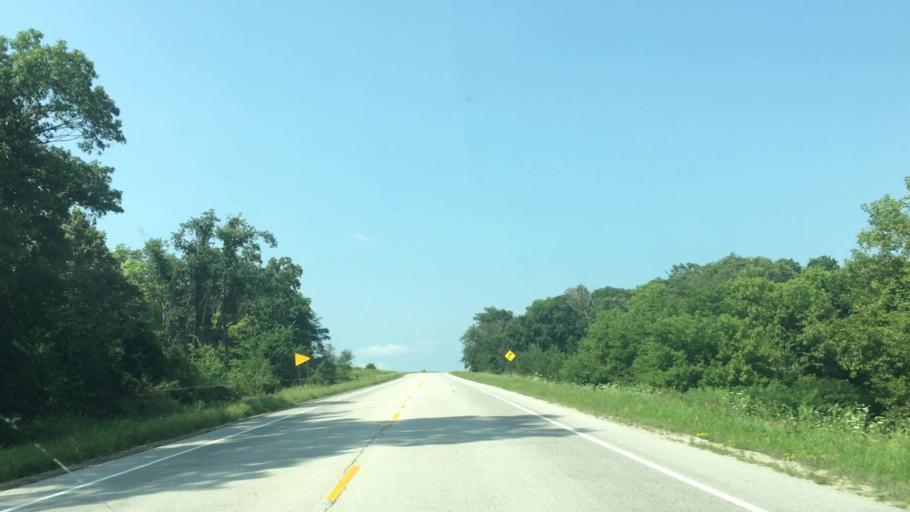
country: US
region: Minnesota
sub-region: Fillmore County
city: Harmony
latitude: 43.6379
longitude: -91.9300
